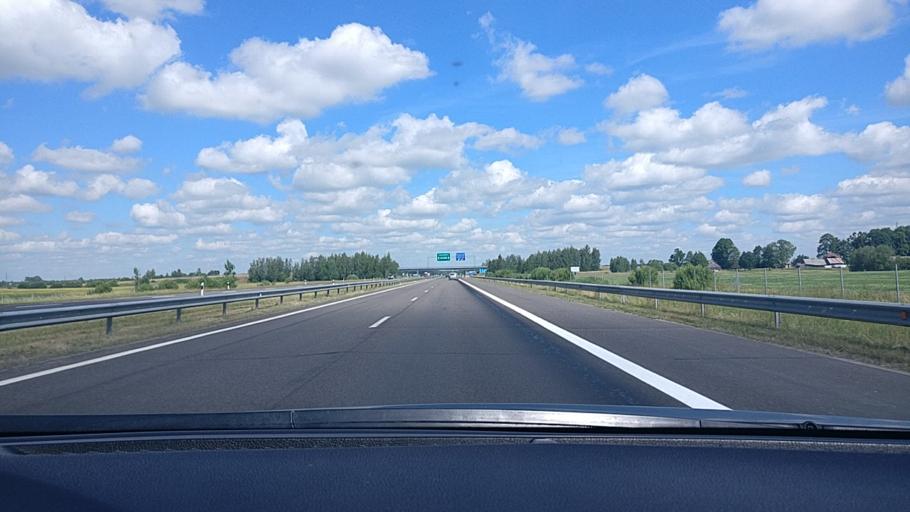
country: LT
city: Sirvintos
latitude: 55.0108
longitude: 24.9157
